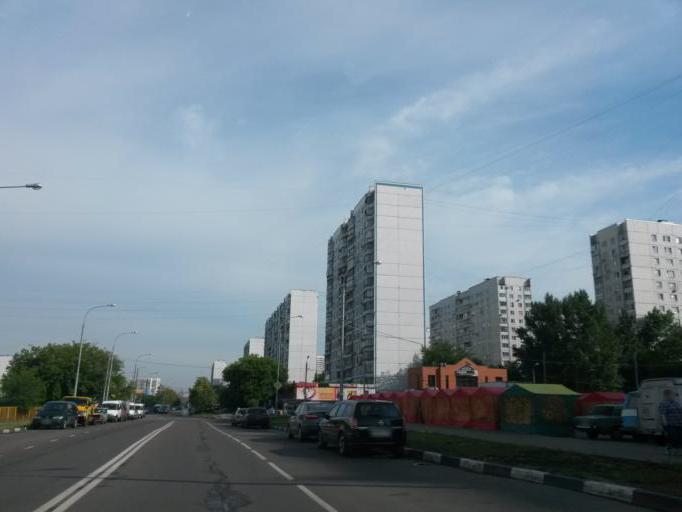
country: RU
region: Moscow
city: Brateyevo
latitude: 55.6345
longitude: 37.7646
